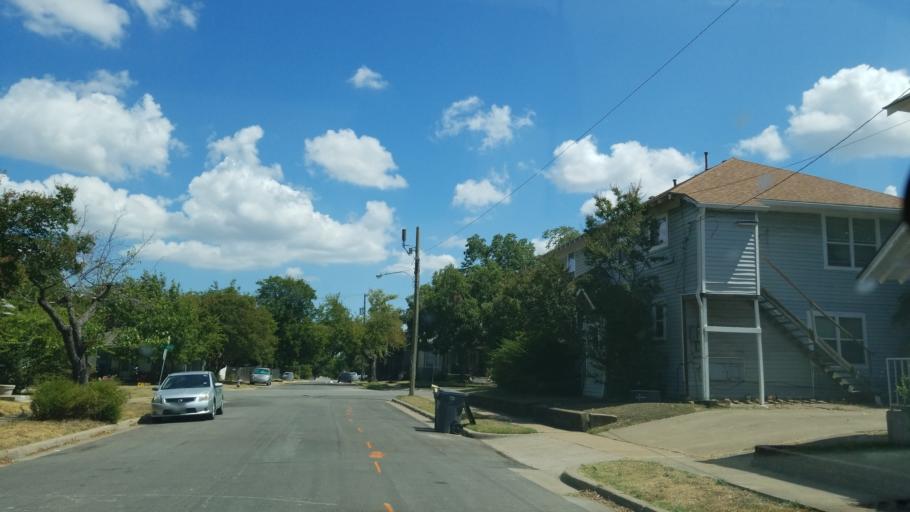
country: US
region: Texas
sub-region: Dallas County
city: Dallas
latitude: 32.7538
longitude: -96.8297
